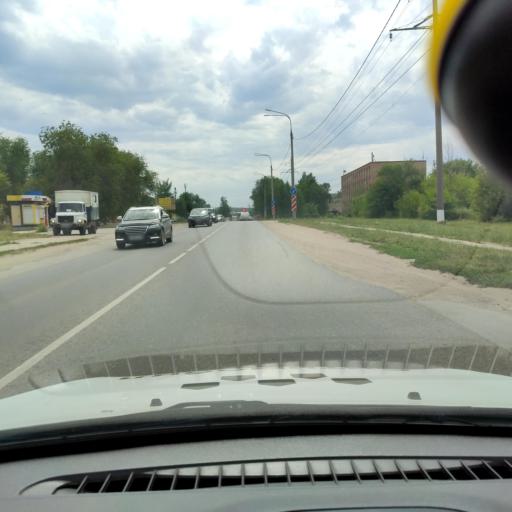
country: RU
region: Samara
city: Zhigulevsk
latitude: 53.4053
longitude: 49.5217
